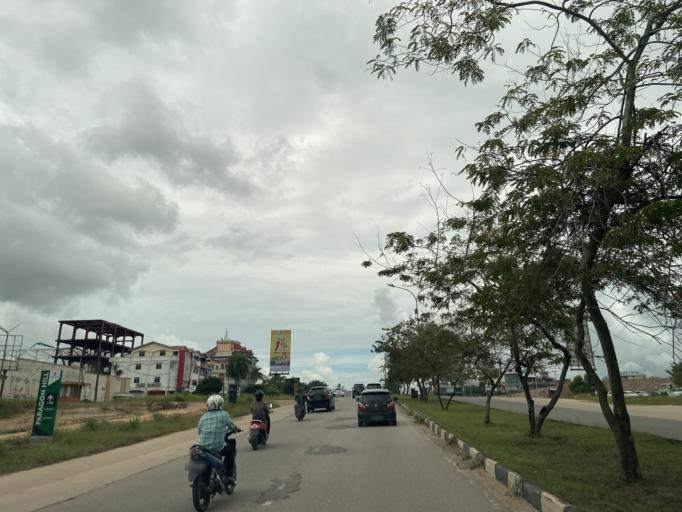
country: SG
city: Singapore
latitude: 1.1287
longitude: 104.0305
